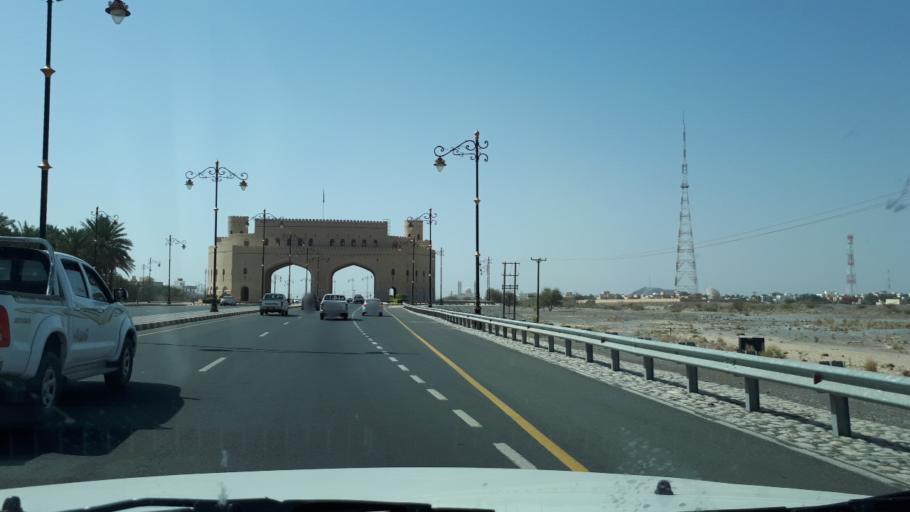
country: OM
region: Muhafazat ad Dakhiliyah
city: Nizwa
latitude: 22.8796
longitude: 57.5260
